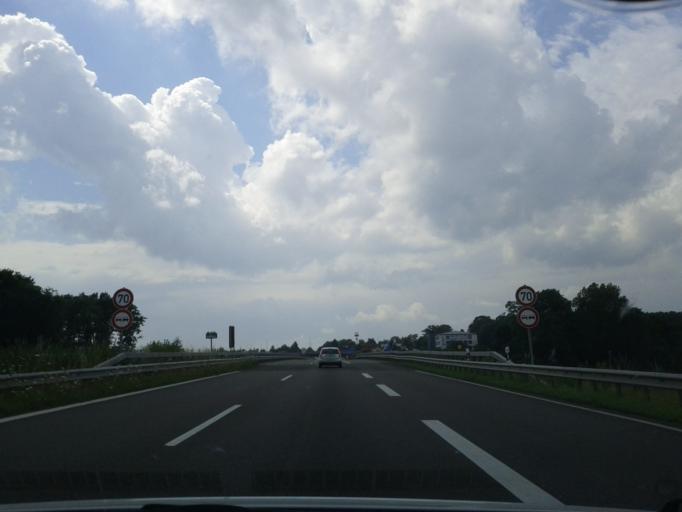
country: DE
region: Lower Saxony
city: Agathenburg
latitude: 53.5812
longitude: 9.5073
